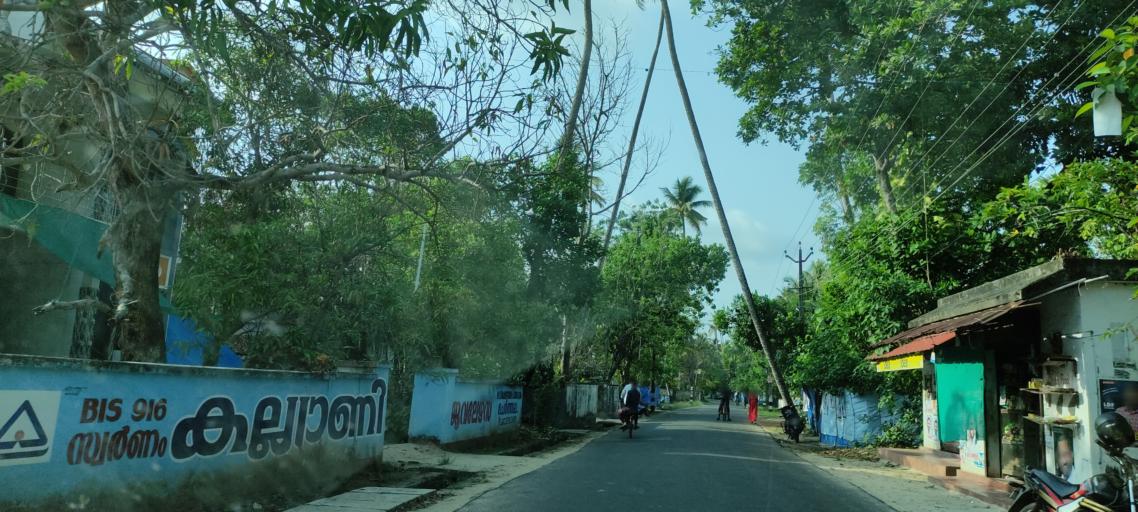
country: IN
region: Kerala
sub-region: Alappuzha
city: Vayalar
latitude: 9.7229
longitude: 76.2872
